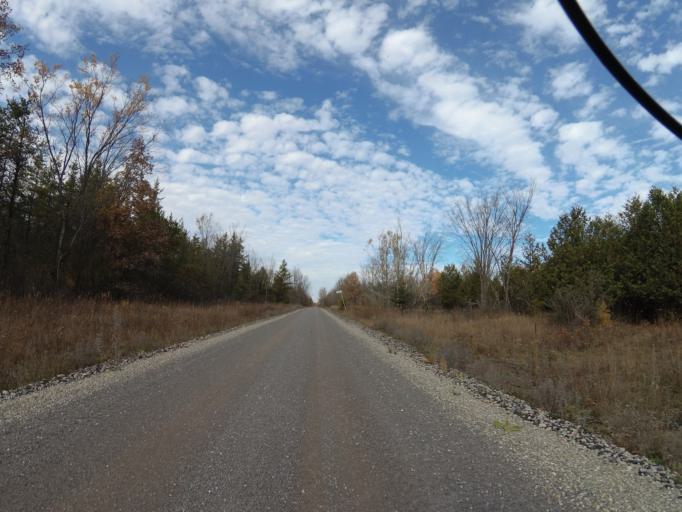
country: CA
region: Ontario
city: Carleton Place
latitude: 45.0713
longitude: -76.0991
